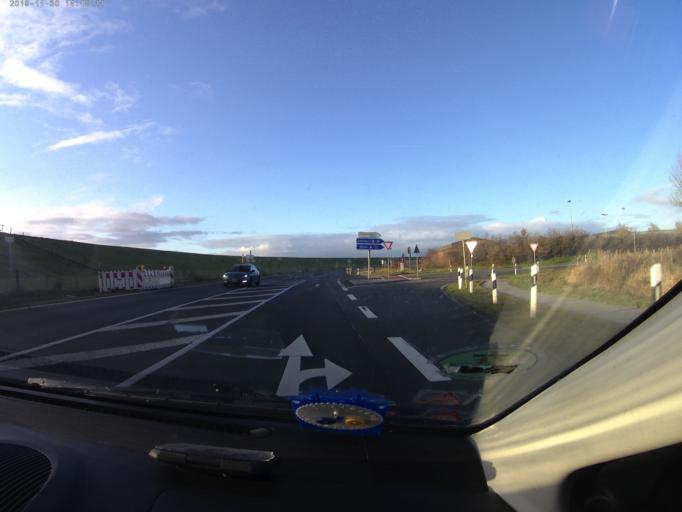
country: DE
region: Lower Saxony
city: Jemgum
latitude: 53.2349
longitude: 7.4109
